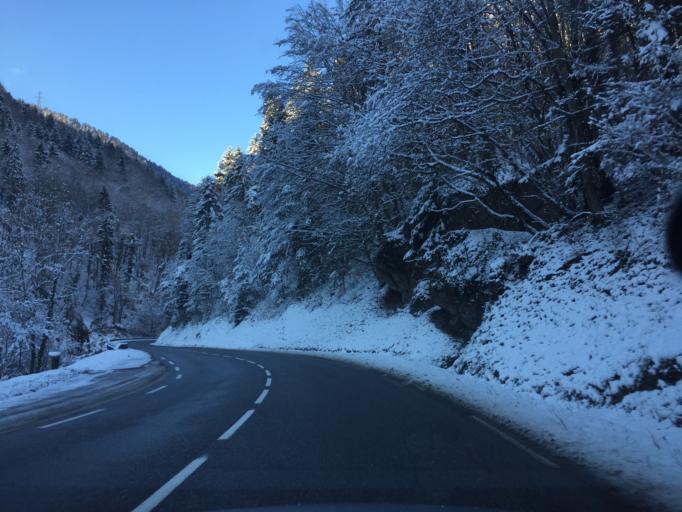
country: FR
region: Rhone-Alpes
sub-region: Departement de la Haute-Savoie
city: Feternes
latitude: 46.3379
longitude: 6.5692
